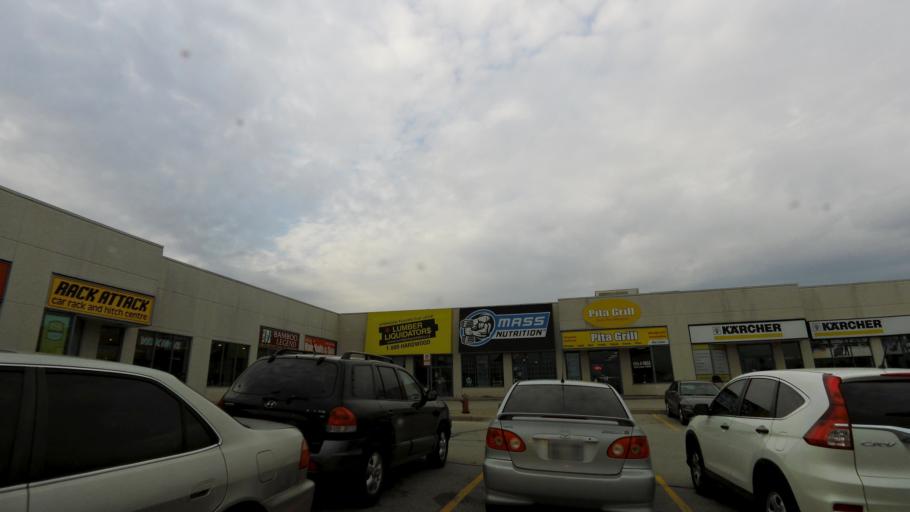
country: CA
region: Ontario
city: Mississauga
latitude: 43.5204
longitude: -79.6862
